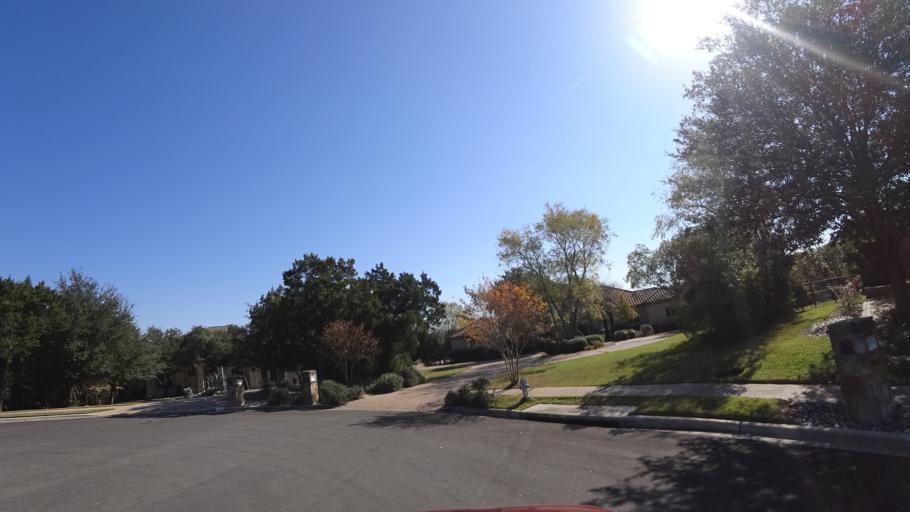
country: US
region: Texas
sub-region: Travis County
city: Lost Creek
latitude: 30.3806
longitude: -97.8482
